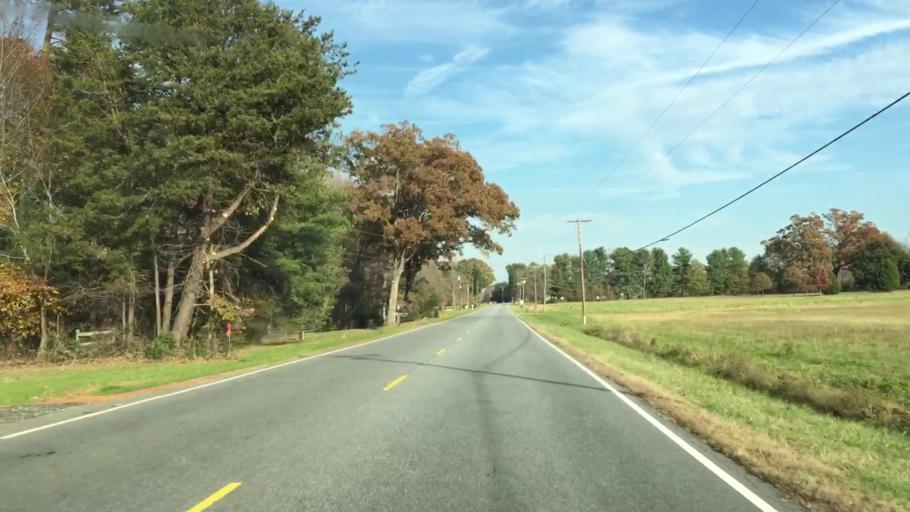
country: US
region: North Carolina
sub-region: Guilford County
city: Summerfield
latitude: 36.2564
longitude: -79.8817
